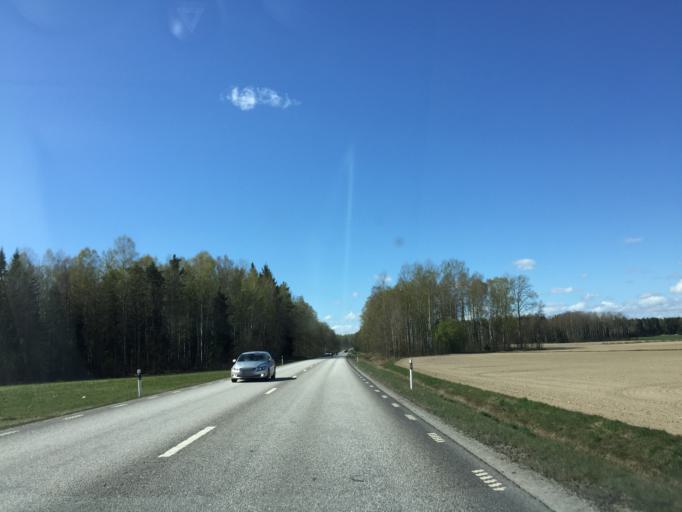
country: SE
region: OErebro
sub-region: Hallsbergs Kommun
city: Skollersta
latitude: 59.1307
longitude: 15.3061
